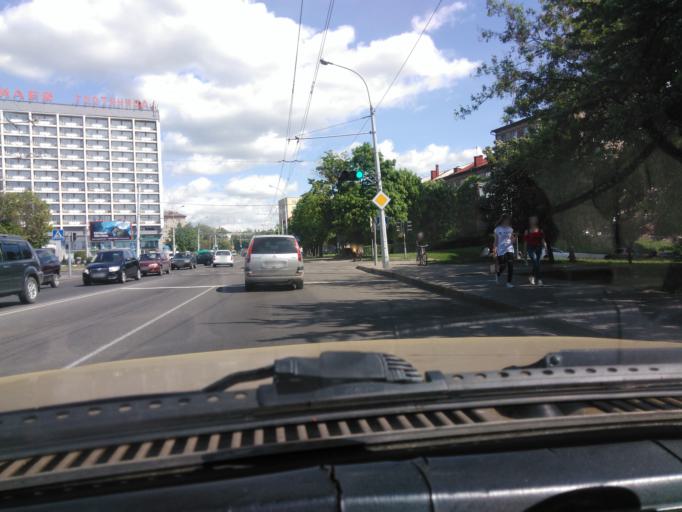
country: BY
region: Mogilev
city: Mahilyow
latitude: 53.9100
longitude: 30.3305
